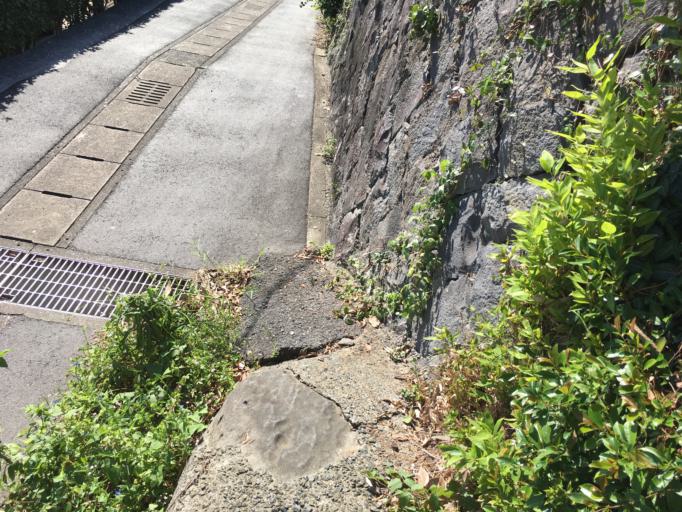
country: JP
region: Kumamoto
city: Kumamoto
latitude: 32.7927
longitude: 130.6687
